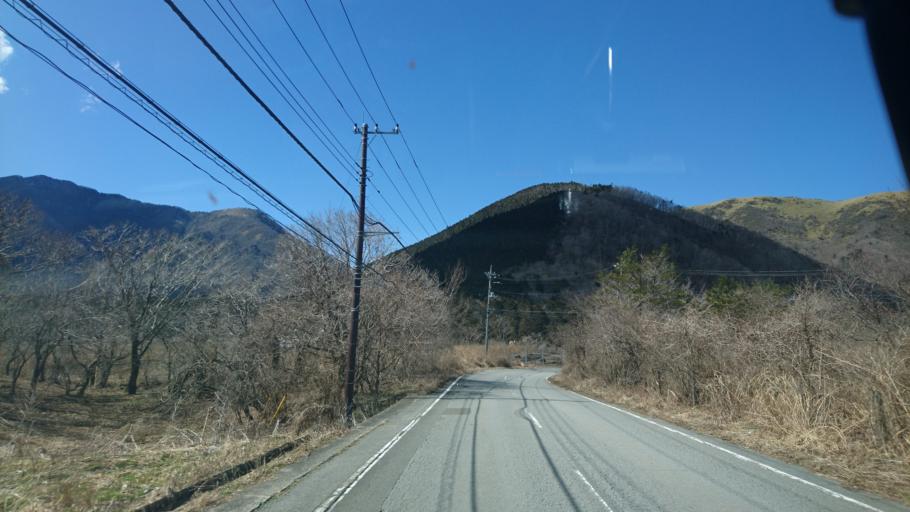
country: JP
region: Yamanashi
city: Fujikawaguchiko
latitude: 35.4321
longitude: 138.5983
